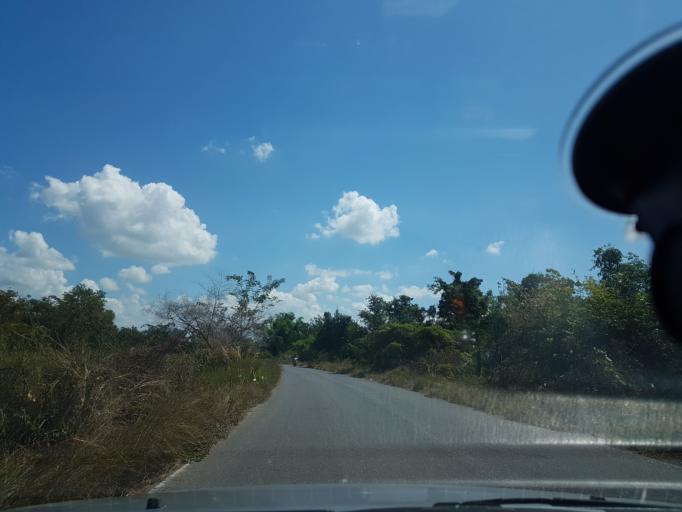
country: TH
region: Lop Buri
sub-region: Amphoe Tha Luang
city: Tha Luang
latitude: 15.0046
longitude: 101.0003
